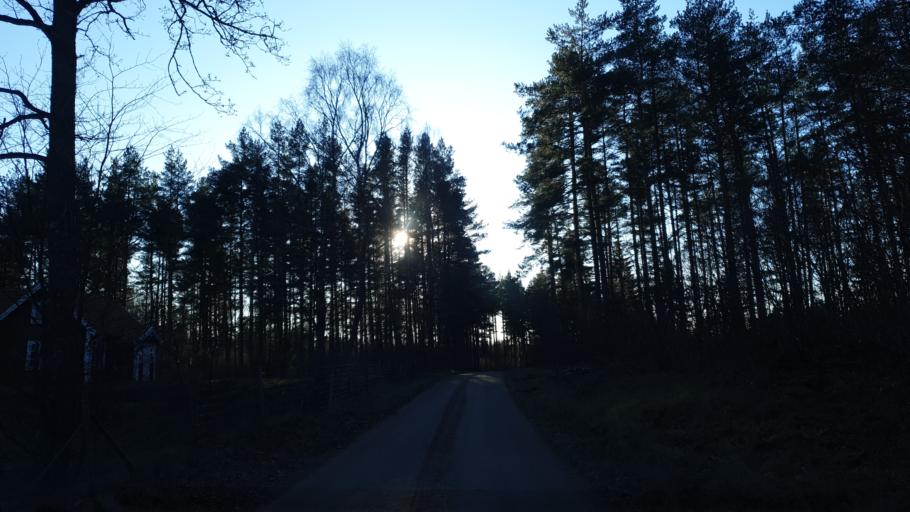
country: SE
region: Blekinge
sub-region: Karlskrona Kommun
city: Nattraby
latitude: 56.2584
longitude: 15.4113
